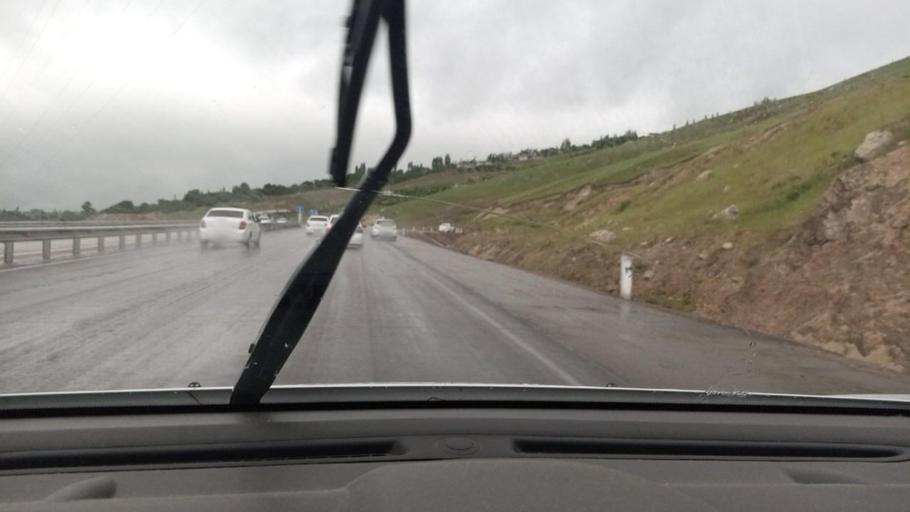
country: UZ
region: Toshkent
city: Angren
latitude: 41.0728
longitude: 70.2700
